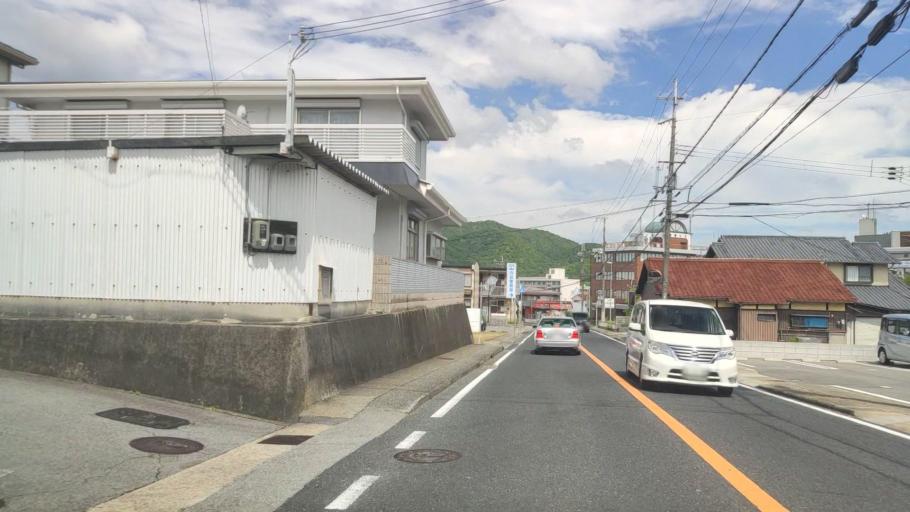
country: JP
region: Hyogo
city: Nishiwaki
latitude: 34.9917
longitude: 134.9707
